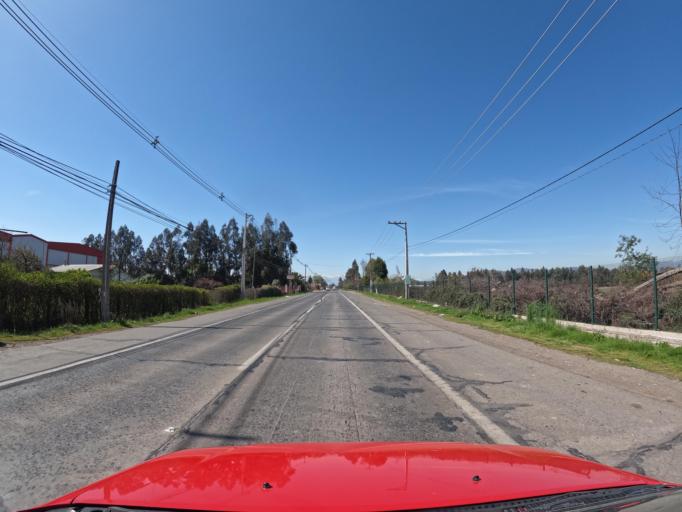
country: CL
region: Maule
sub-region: Provincia de Curico
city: Curico
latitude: -34.9639
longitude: -71.1829
